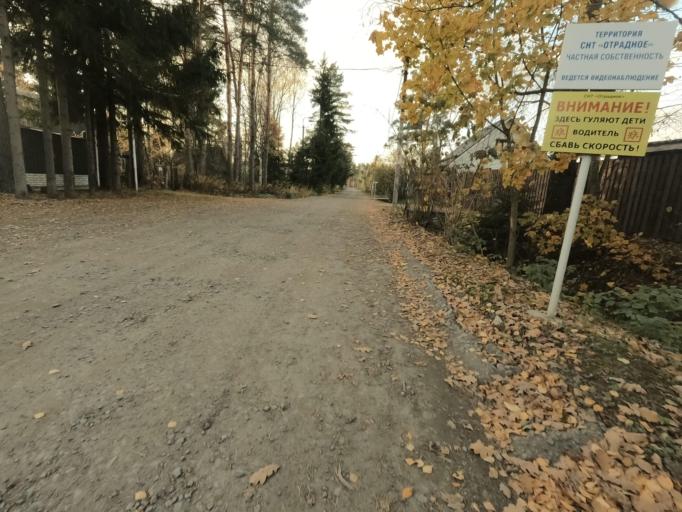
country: RU
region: St.-Petersburg
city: Beloostrov
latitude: 60.1622
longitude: 30.0016
